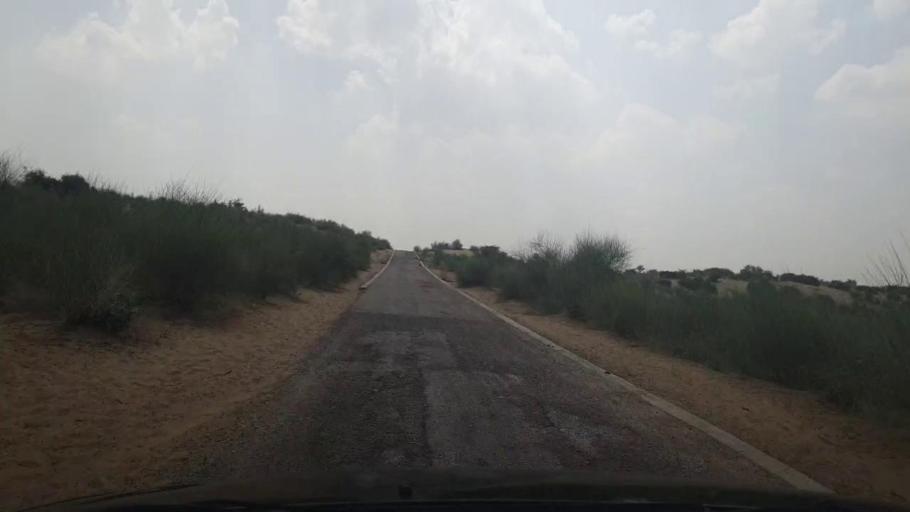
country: PK
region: Sindh
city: Islamkot
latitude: 25.0021
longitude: 70.5005
